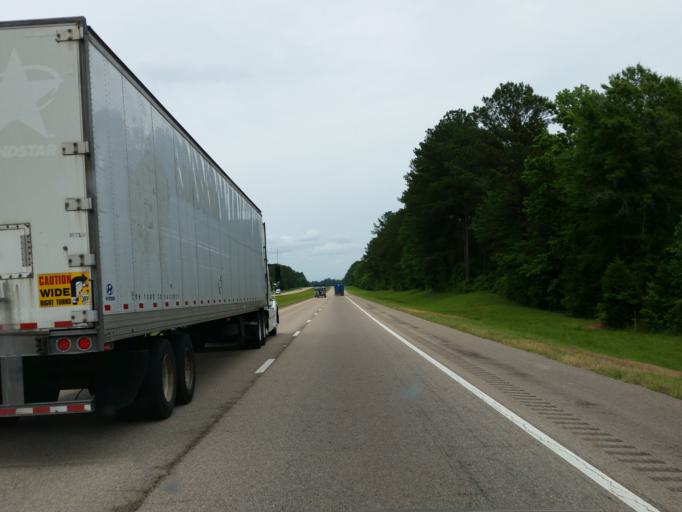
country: US
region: Mississippi
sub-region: Clarke County
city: Stonewall
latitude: 32.0020
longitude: -88.9361
